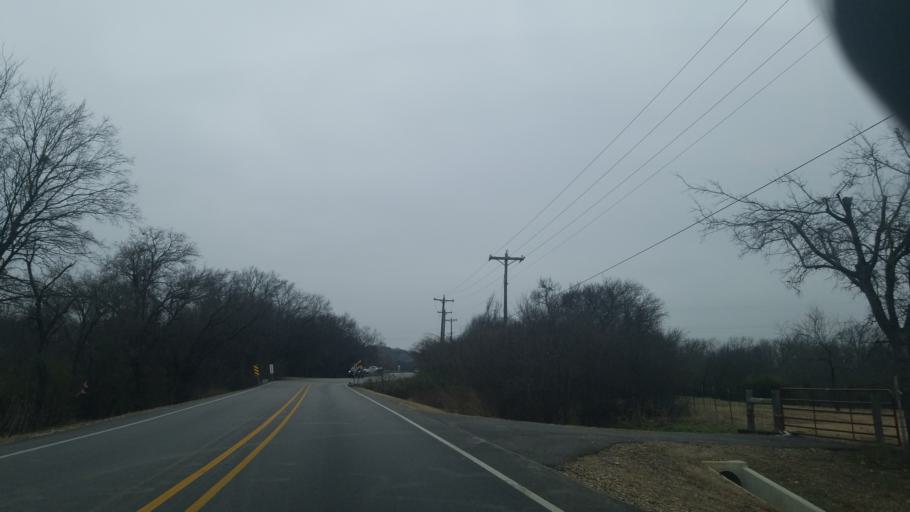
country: US
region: Texas
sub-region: Denton County
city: Argyle
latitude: 33.1538
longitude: -97.1420
